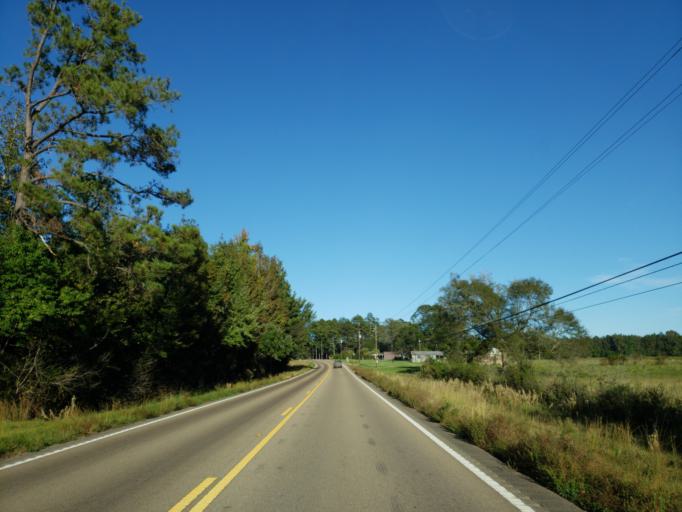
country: US
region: Mississippi
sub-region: Perry County
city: Richton
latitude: 31.3676
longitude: -88.8768
